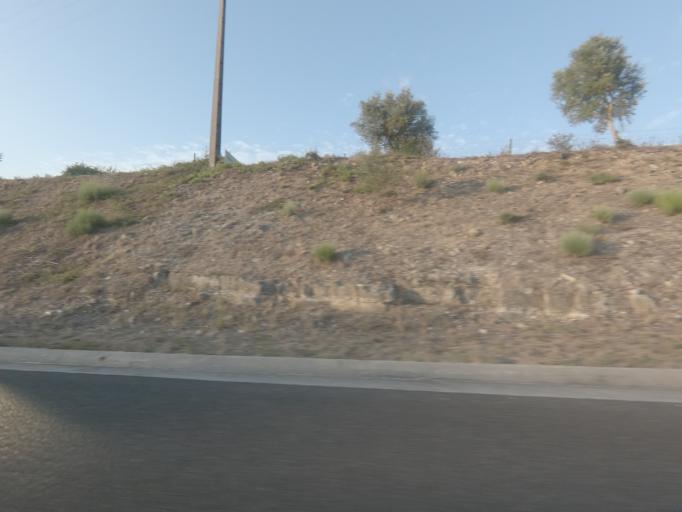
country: PT
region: Leiria
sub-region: Leiria
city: Santa Catarina da Serra
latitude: 39.7027
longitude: -8.7007
